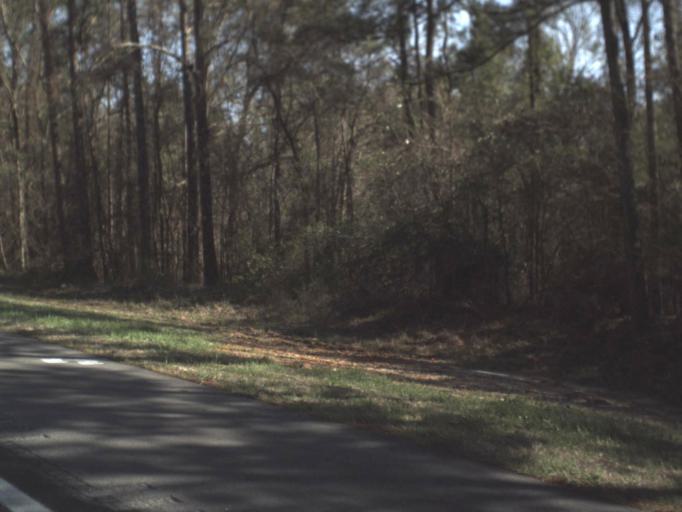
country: US
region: Florida
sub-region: Gadsden County
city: Chattahoochee
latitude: 30.6306
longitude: -84.8668
